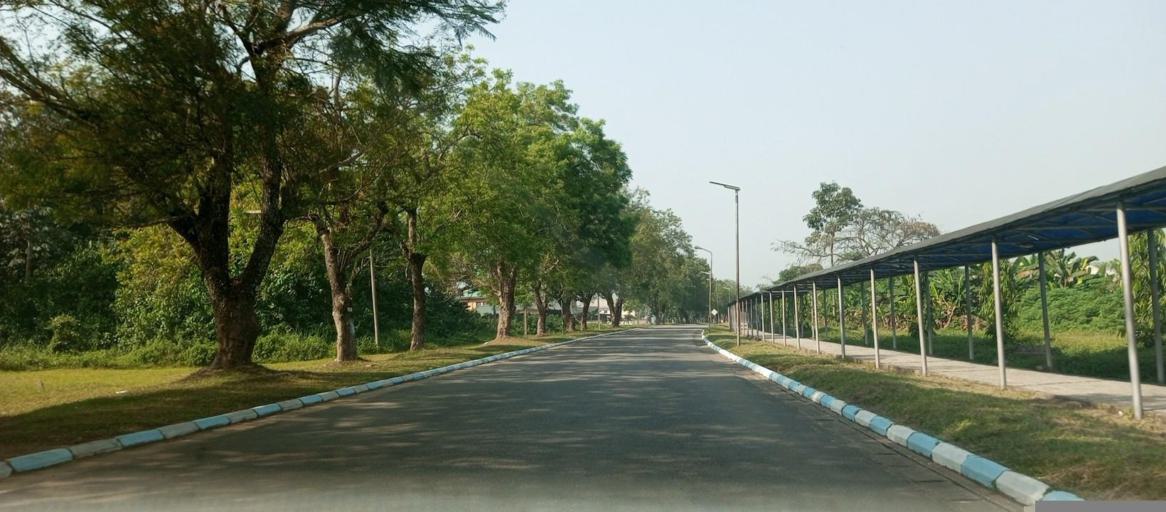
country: NG
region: Rivers
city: Emuoha
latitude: 4.9032
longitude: 6.9121
